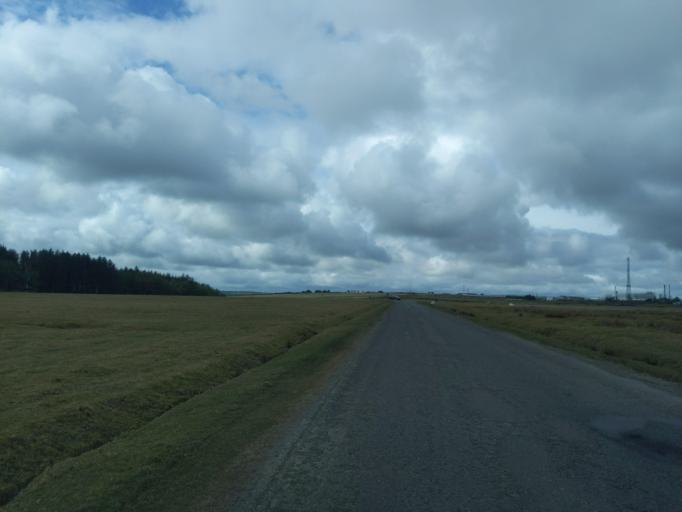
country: GB
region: England
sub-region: Cornwall
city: Camelford
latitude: 50.6383
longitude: -4.6241
